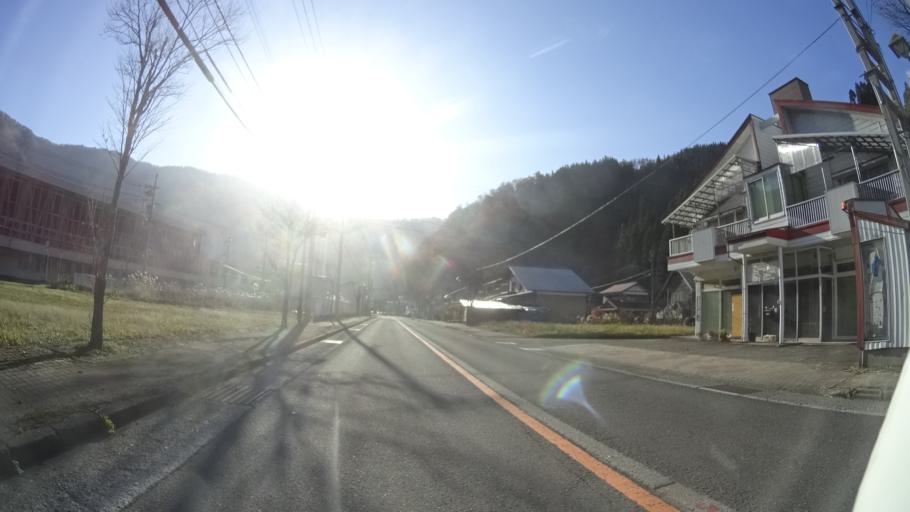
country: JP
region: Fukui
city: Ono
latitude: 35.9028
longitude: 136.6590
